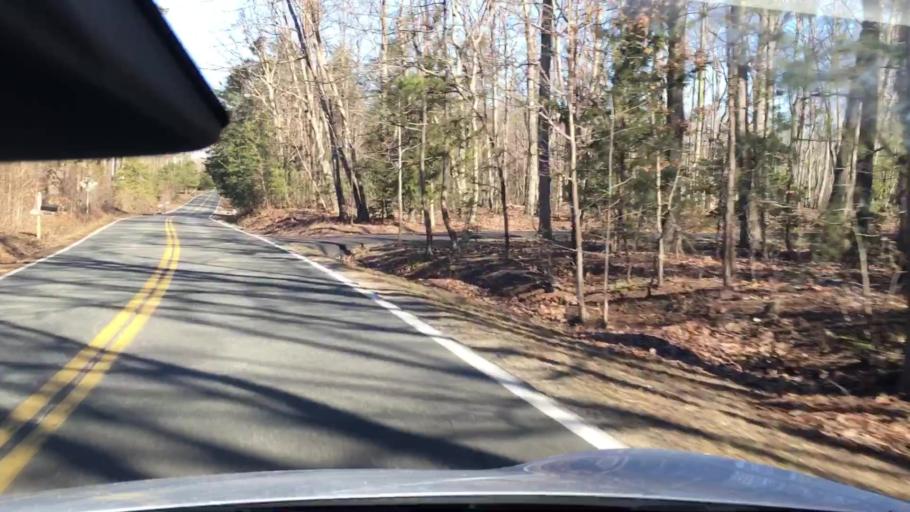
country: US
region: Virginia
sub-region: Powhatan County
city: Powhatan
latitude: 37.5450
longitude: -77.7936
